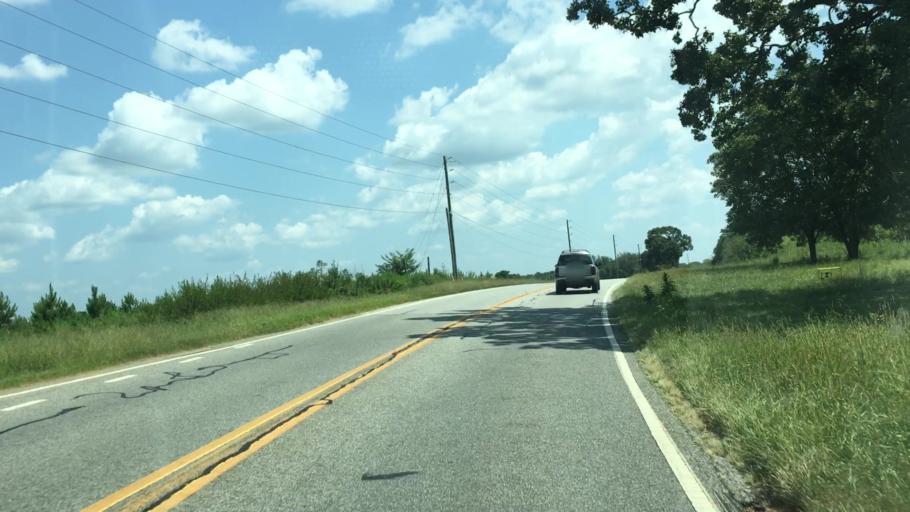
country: US
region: Georgia
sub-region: Barrow County
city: Statham
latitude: 33.9353
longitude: -83.6241
